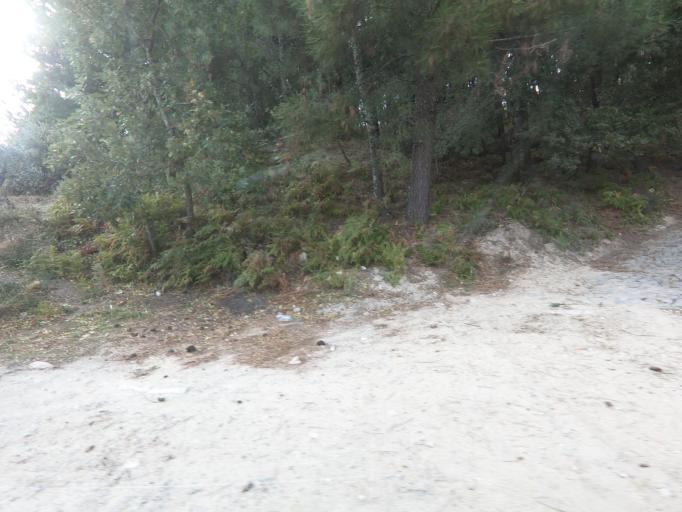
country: PT
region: Vila Real
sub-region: Vila Real
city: Vila Real
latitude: 41.3264
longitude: -7.7749
